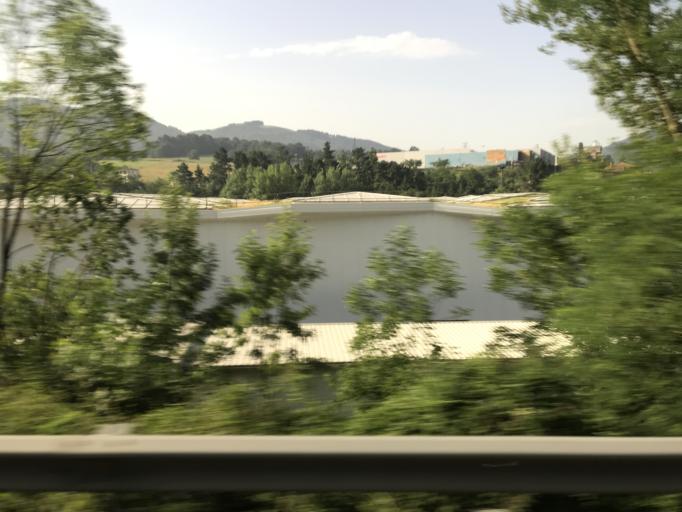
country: ES
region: Basque Country
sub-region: Provincia de Guipuzcoa
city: Idiazabal
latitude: 43.0252
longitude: -2.2283
